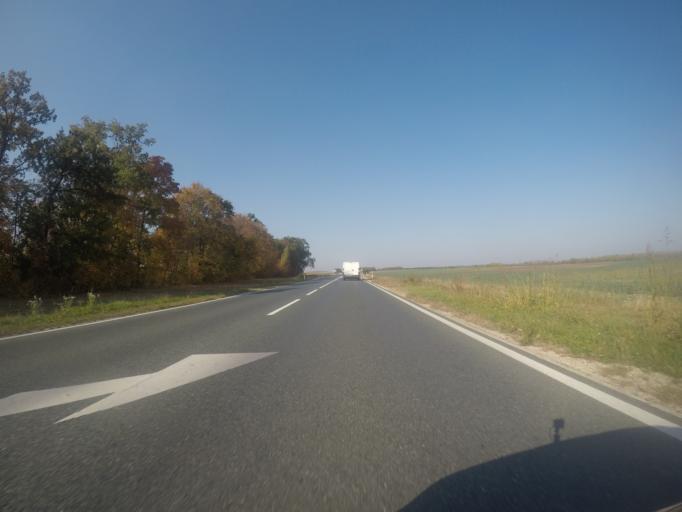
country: HU
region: Tolna
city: Madocsa
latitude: 46.7239
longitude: 18.8843
